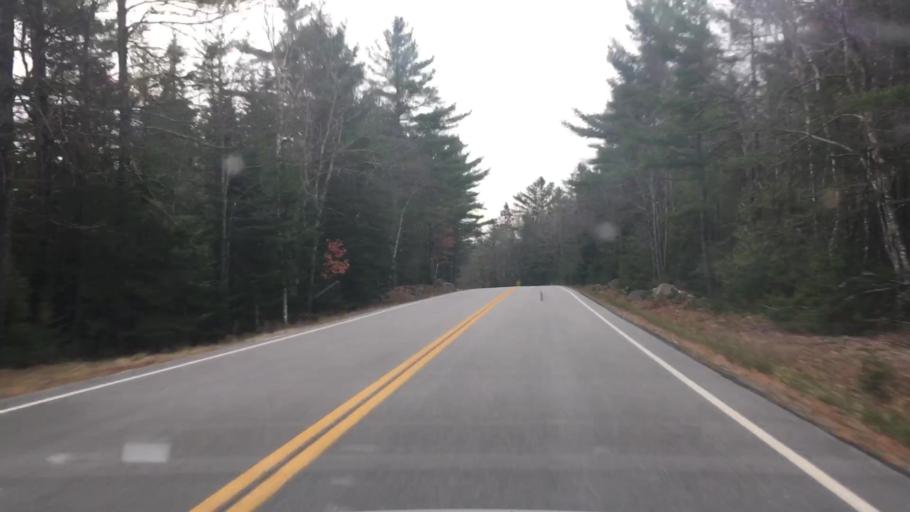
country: US
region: Maine
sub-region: Hancock County
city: Penobscot
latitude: 44.5069
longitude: -68.6557
